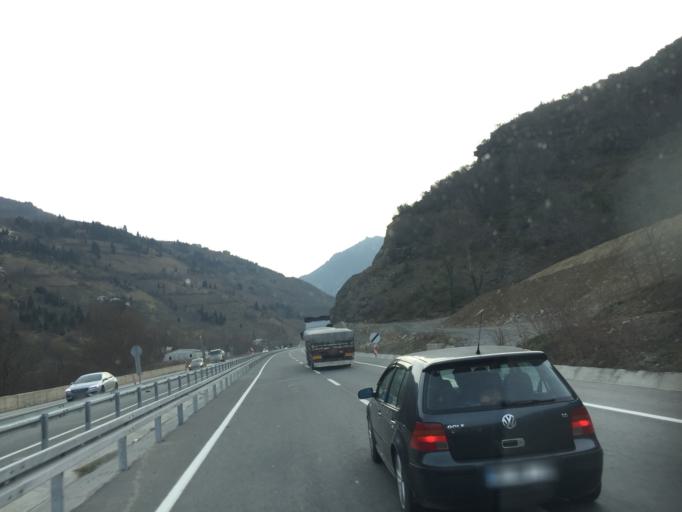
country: TR
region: Trabzon
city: Macka
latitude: 40.7914
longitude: 39.5809
